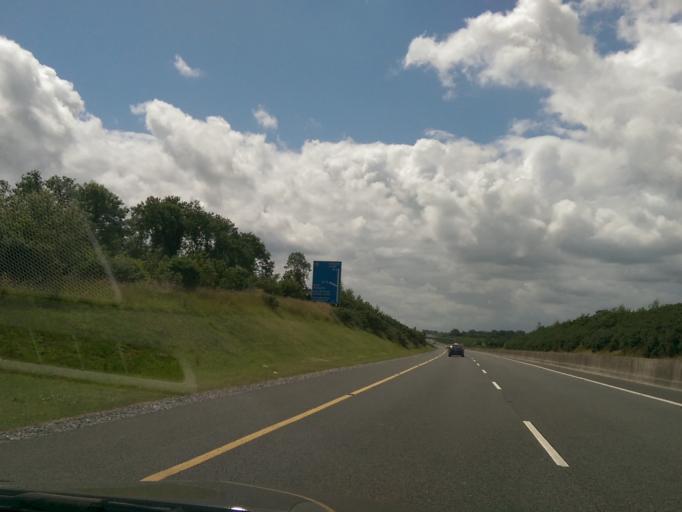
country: IE
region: Munster
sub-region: County Cork
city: Mitchelstown
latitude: 52.2935
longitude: -8.1953
